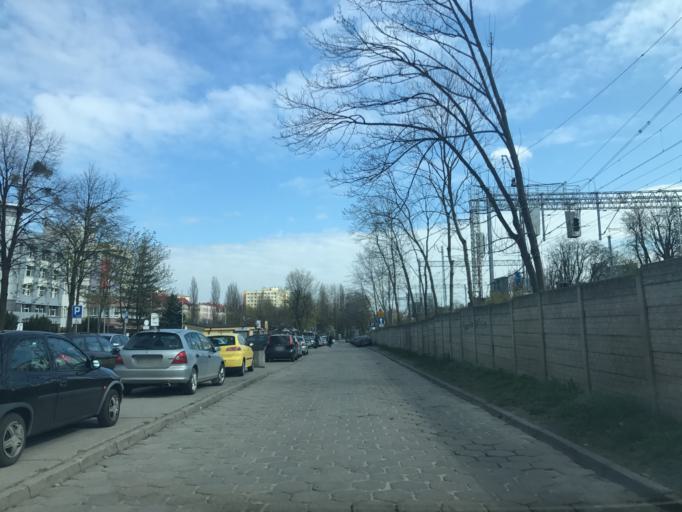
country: PL
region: Pomeranian Voivodeship
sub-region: Gdansk
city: Gdansk
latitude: 54.3794
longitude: 18.6127
